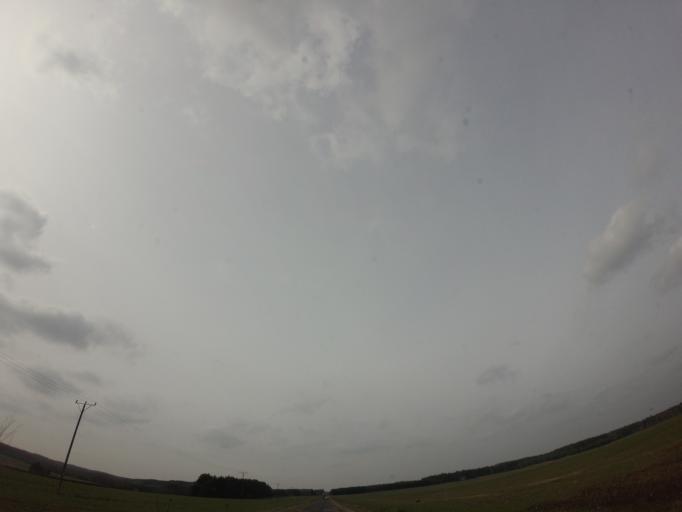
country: PL
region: West Pomeranian Voivodeship
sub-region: Powiat drawski
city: Wierzchowo
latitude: 53.4331
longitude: 16.1926
